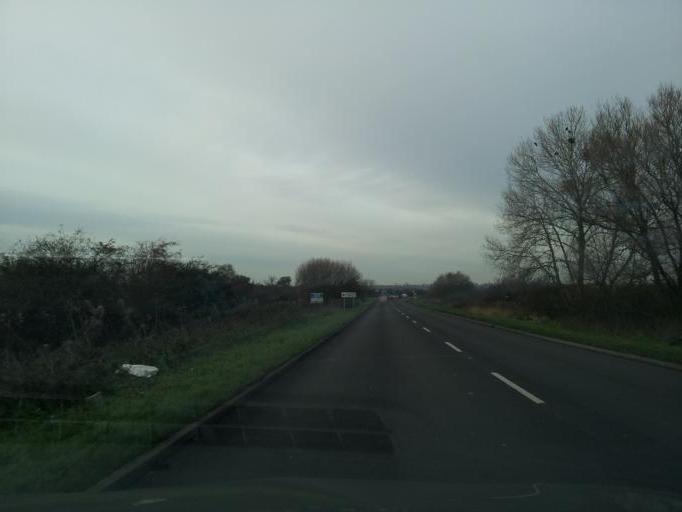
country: GB
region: England
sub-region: Buckinghamshire
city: Aylesbury
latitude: 51.8412
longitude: -0.7732
